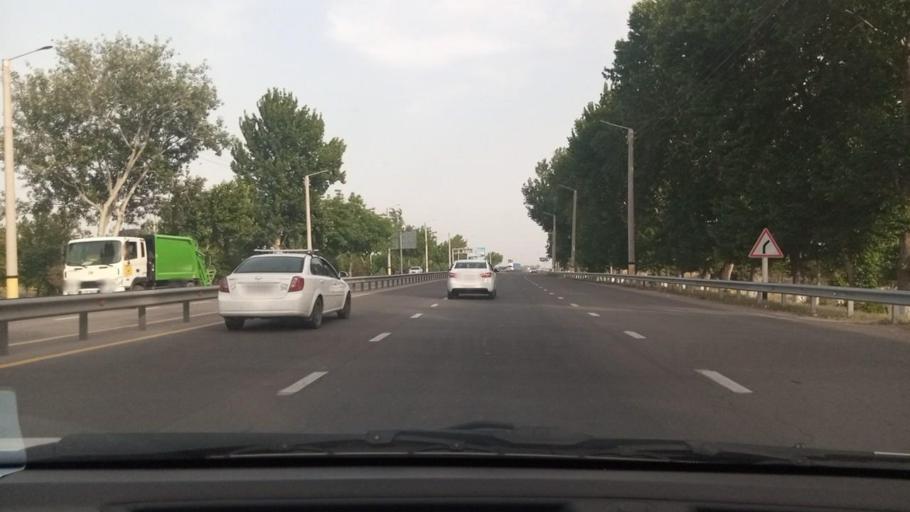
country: UZ
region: Toshkent Shahri
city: Bektemir
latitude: 41.2426
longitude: 69.3986
